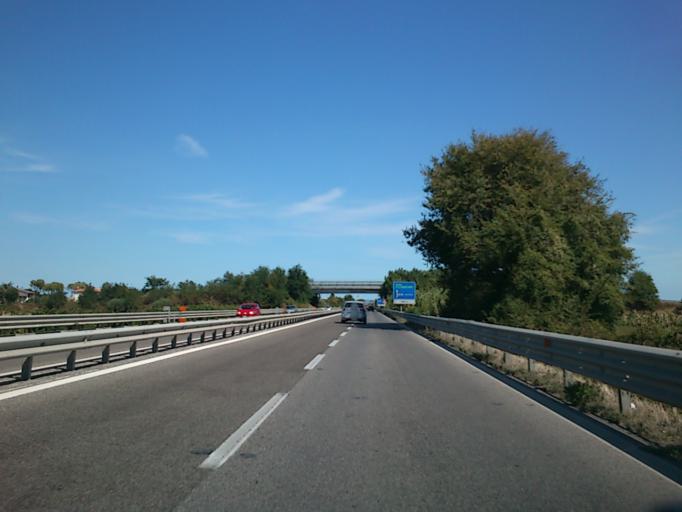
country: IT
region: The Marches
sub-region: Provincia di Pesaro e Urbino
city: Bellocchi
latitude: 43.7823
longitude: 12.9892
